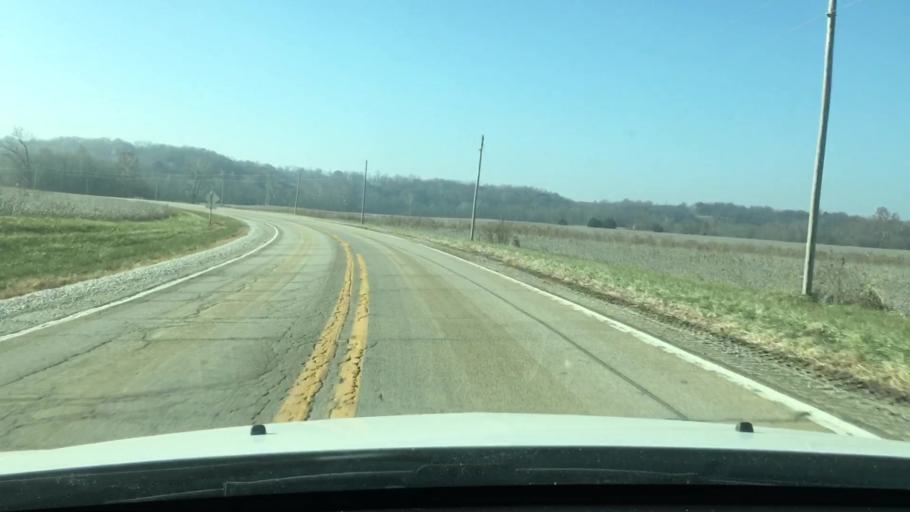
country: US
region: Illinois
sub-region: Mason County
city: Havana
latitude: 40.2782
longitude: -90.1731
